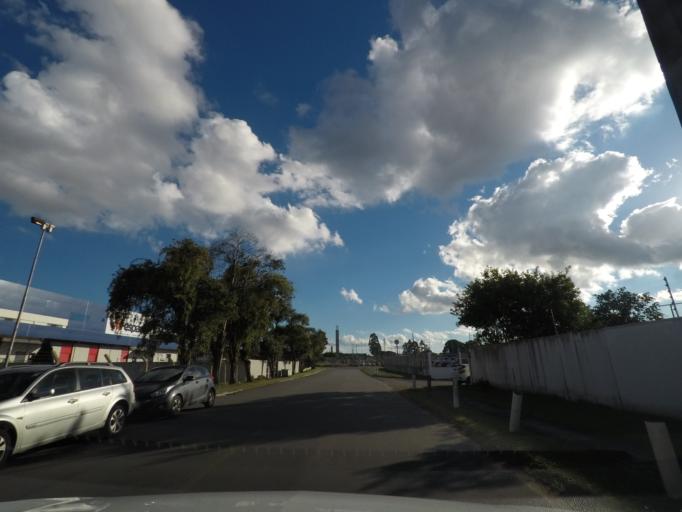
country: BR
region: Parana
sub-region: Curitiba
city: Curitiba
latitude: -25.4835
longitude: -49.2634
